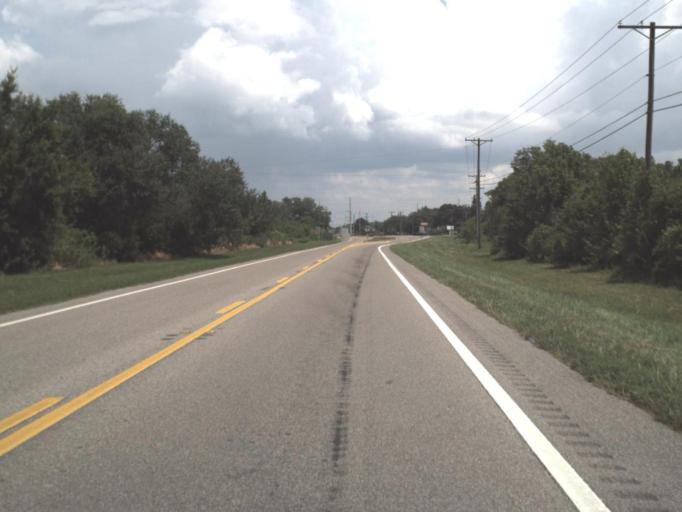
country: US
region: Florida
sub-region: Hillsborough County
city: Sun City Center
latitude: 27.7074
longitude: -82.3366
